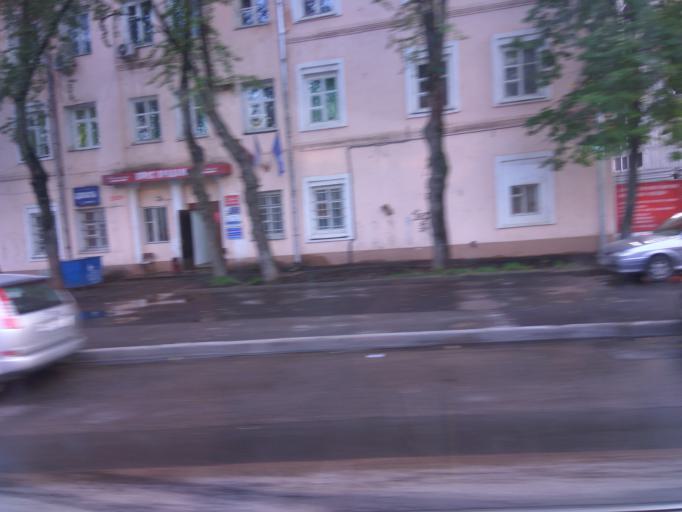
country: RU
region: Moskovskaya
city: Bogorodskoye
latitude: 55.8004
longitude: 37.7123
